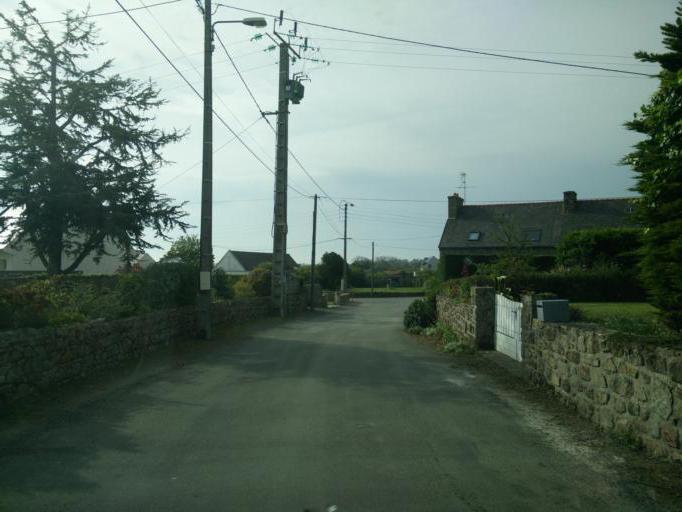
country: FR
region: Brittany
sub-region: Departement des Cotes-d'Armor
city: Pleubian
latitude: 48.8632
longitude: -3.0978
